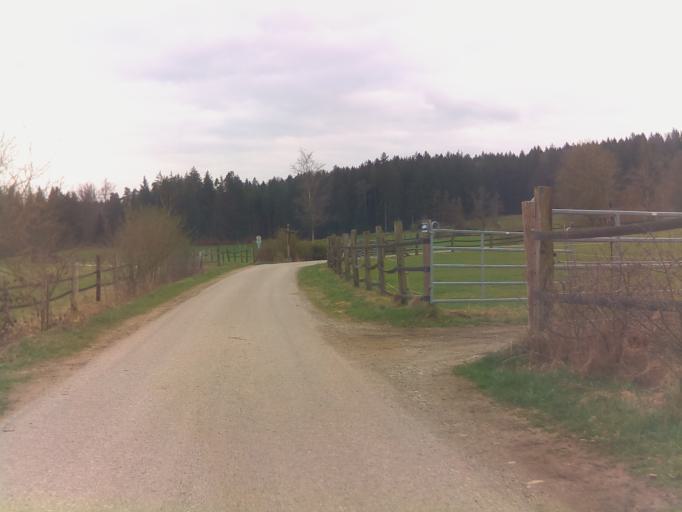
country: DE
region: Bavaria
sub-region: Upper Bavaria
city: Utting am Ammersee
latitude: 48.0160
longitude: 11.0596
